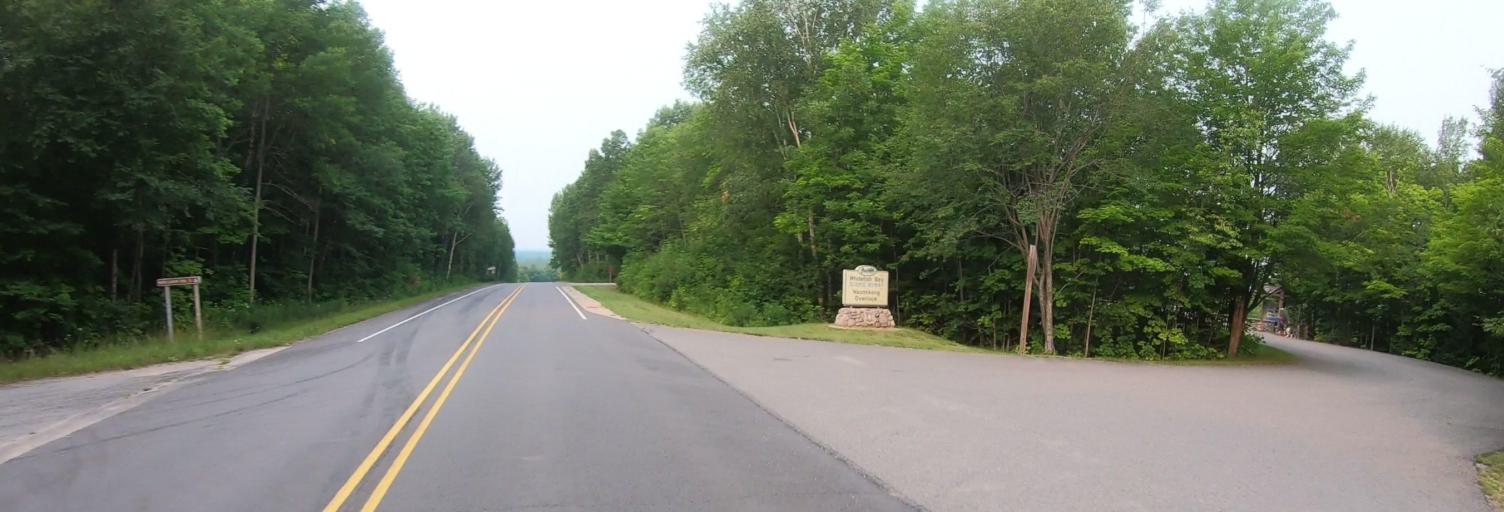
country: US
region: Michigan
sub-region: Luce County
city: Newberry
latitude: 46.4731
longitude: -84.9565
